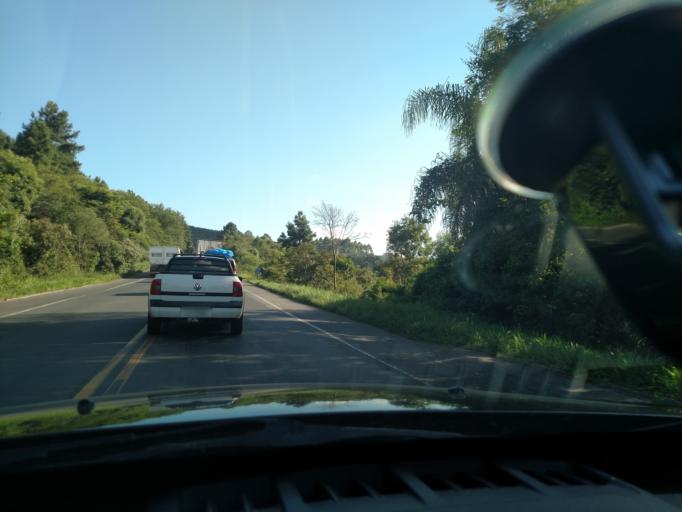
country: BR
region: Santa Catarina
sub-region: Otacilio Costa
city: Otacilio Costa
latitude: -27.2701
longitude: -50.0621
